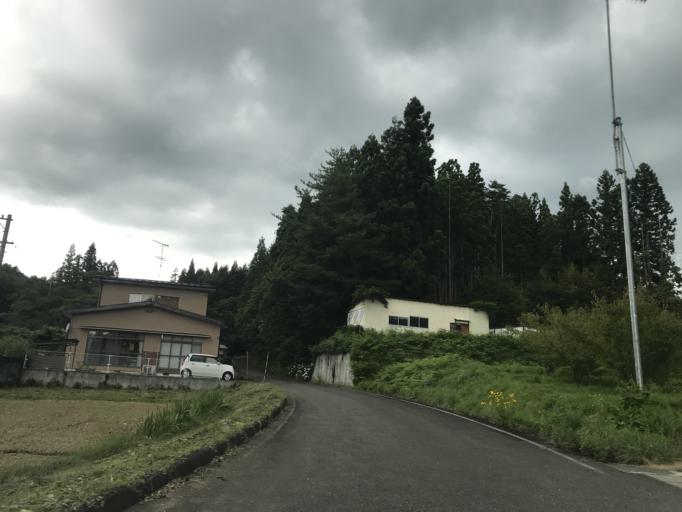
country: JP
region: Iwate
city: Ichinoseki
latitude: 38.9537
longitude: 141.0481
